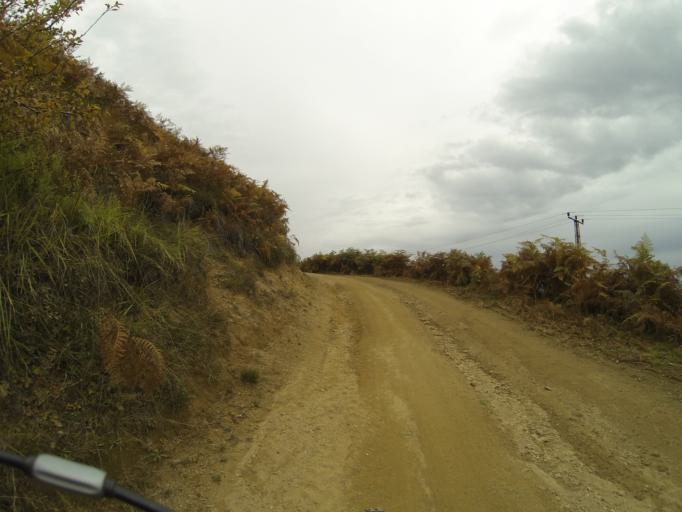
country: RO
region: Gorj
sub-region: Comuna Pades
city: Closani
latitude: 45.1161
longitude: 22.8496
